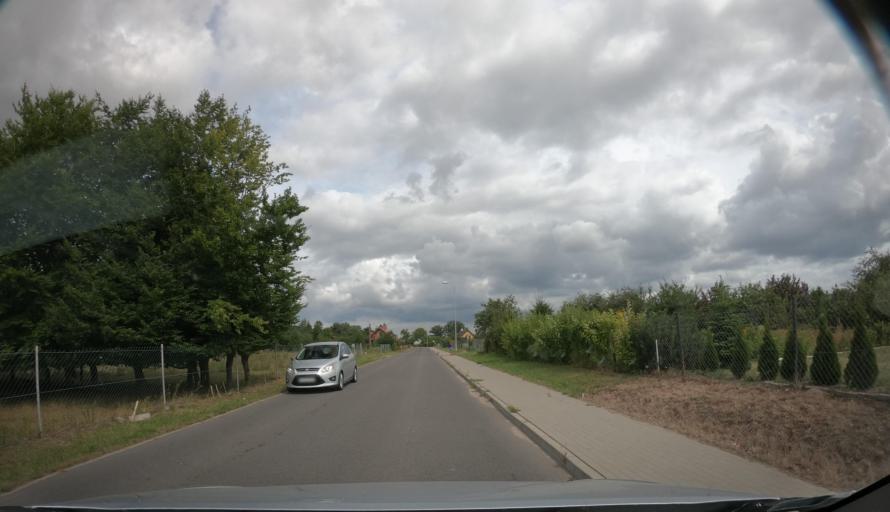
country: PL
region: West Pomeranian Voivodeship
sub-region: Koszalin
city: Koszalin
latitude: 54.1401
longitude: 16.0824
